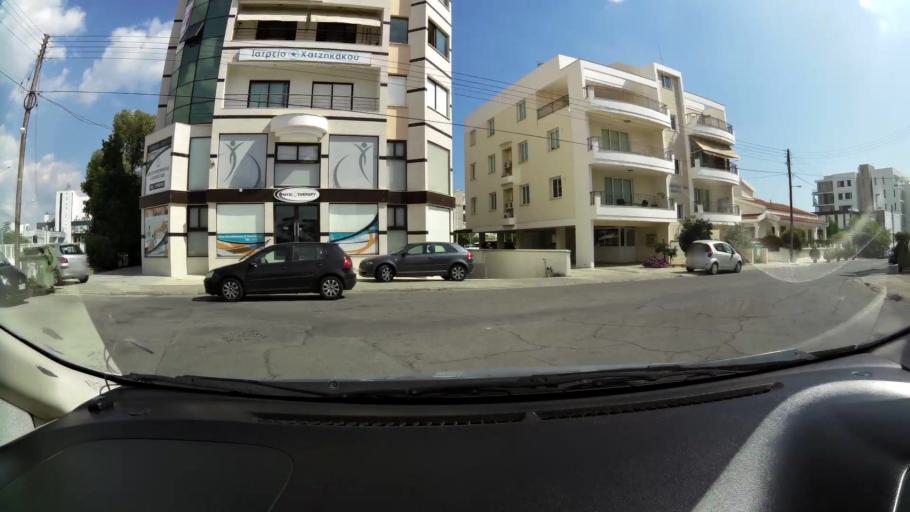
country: CY
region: Larnaka
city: Larnaca
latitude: 34.9165
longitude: 33.6053
